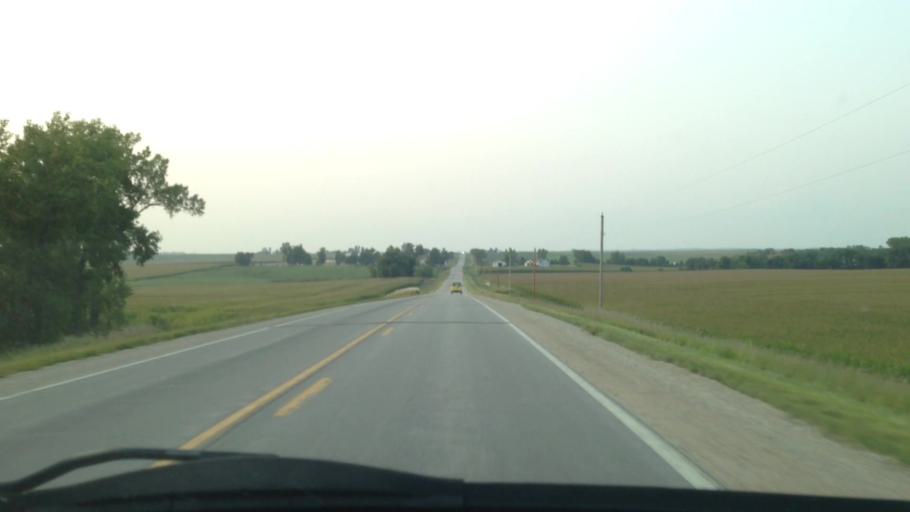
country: US
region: Iowa
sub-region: Benton County
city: Atkins
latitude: 41.9986
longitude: -91.8734
